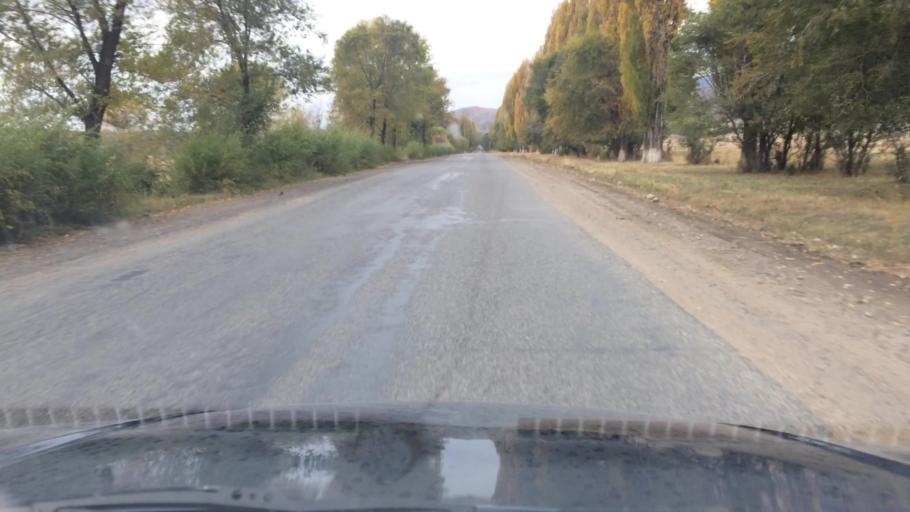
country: KG
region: Ysyk-Koel
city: Pokrovka
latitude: 42.7376
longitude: 77.9267
